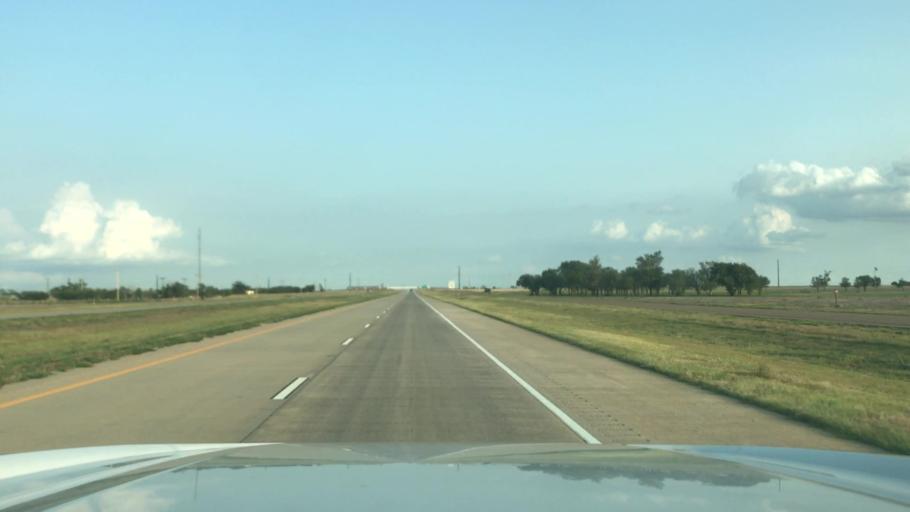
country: US
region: Texas
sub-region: Hale County
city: Seth Ward
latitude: 34.3622
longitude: -101.7612
